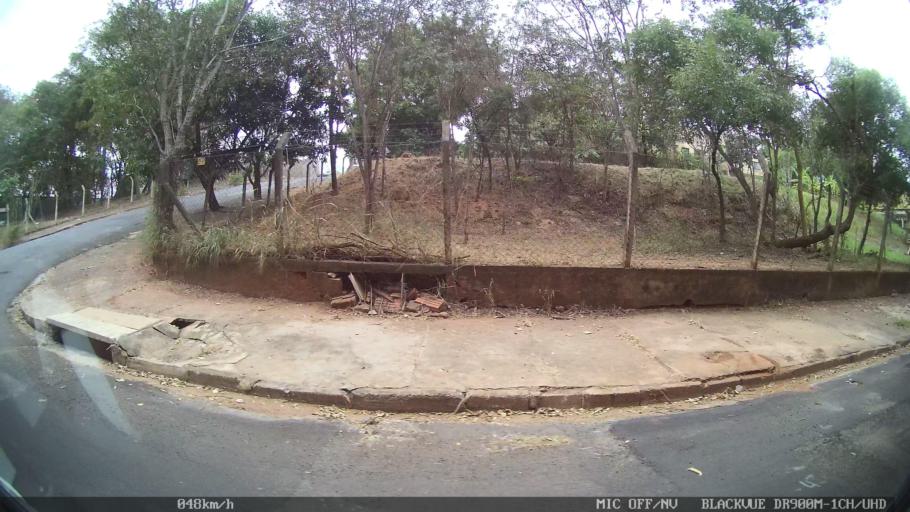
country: BR
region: Sao Paulo
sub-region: Sao Jose Do Rio Preto
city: Sao Jose do Rio Preto
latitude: -20.8187
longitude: -49.4311
